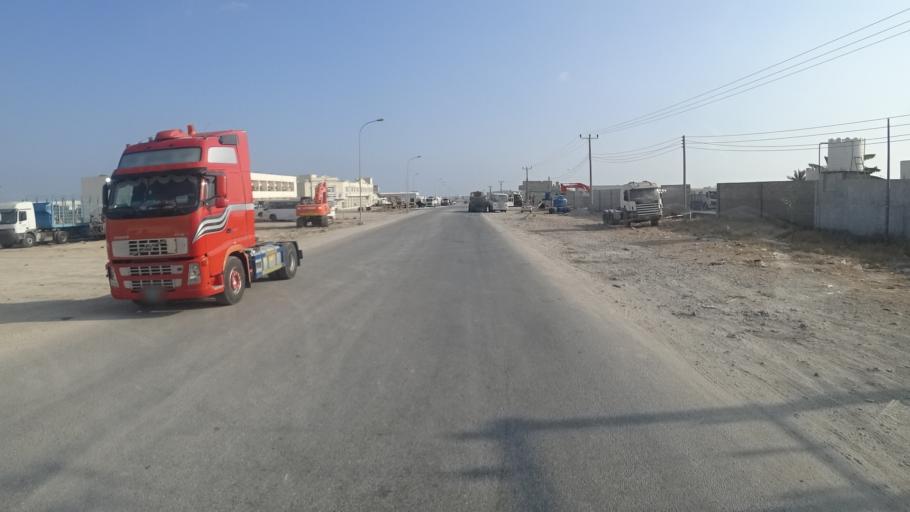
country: OM
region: Zufar
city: Salalah
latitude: 17.0349
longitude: 54.0431
